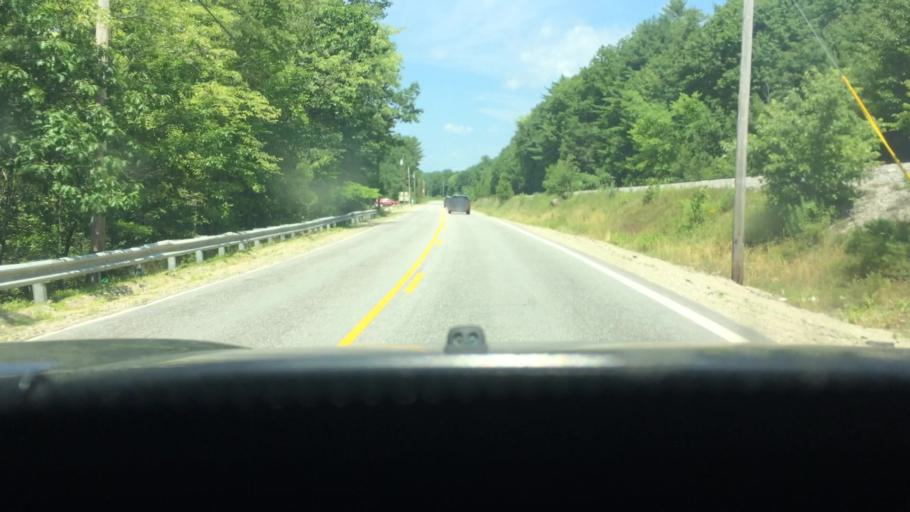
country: US
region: Maine
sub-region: Androscoggin County
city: Mechanic Falls
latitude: 44.1252
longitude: -70.4333
